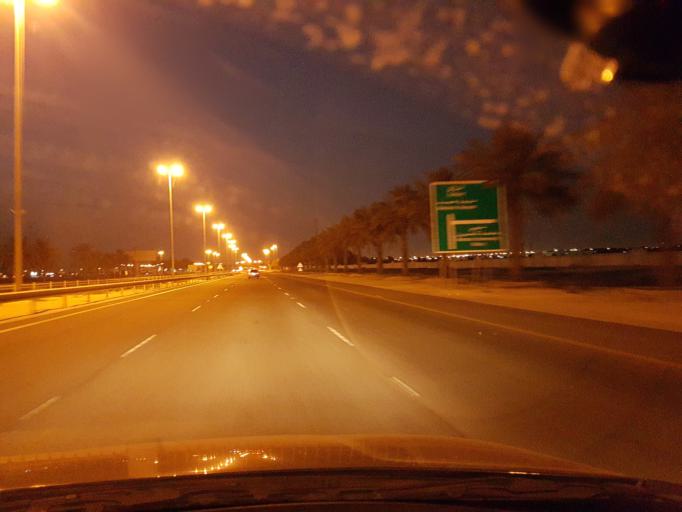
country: BH
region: Central Governorate
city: Dar Kulayb
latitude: 26.0440
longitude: 50.5000
